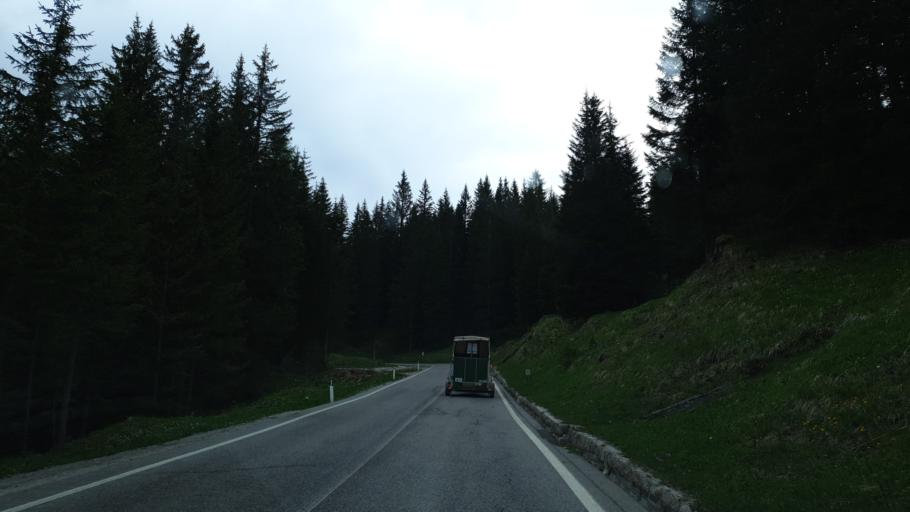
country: IT
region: Veneto
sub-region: Provincia di Belluno
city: San Vito
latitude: 46.5608
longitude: 12.2469
